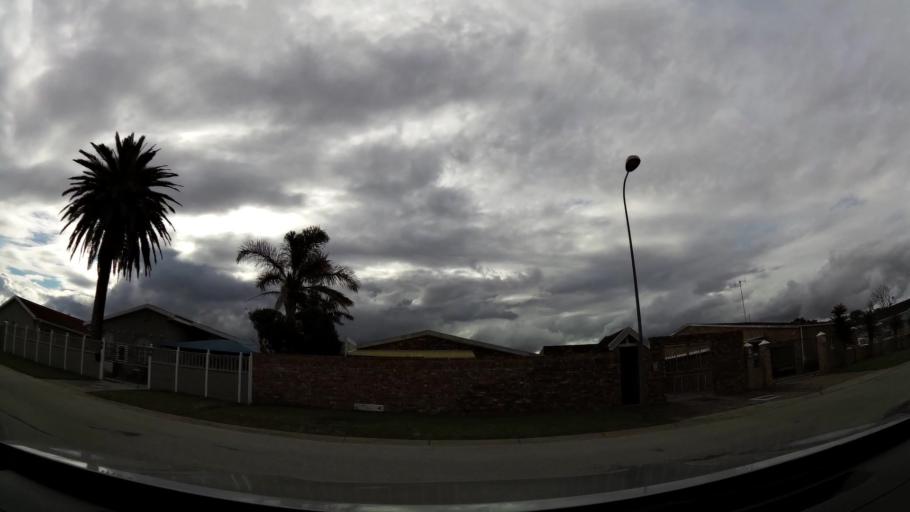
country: ZA
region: Eastern Cape
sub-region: Nelson Mandela Bay Metropolitan Municipality
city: Port Elizabeth
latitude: -33.9384
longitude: 25.4739
